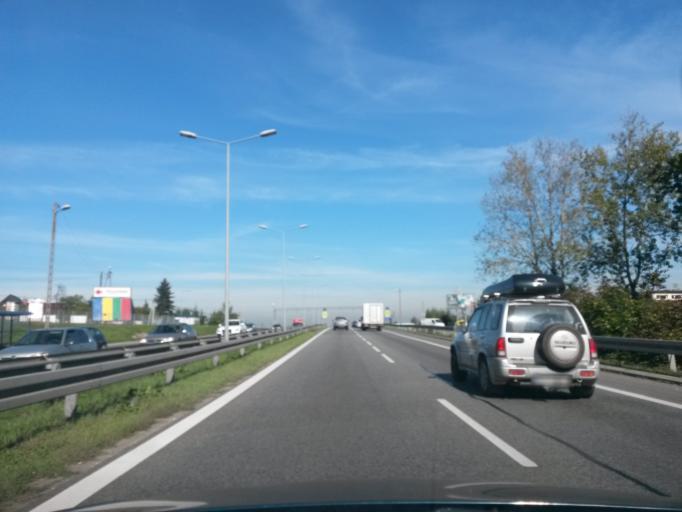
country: PL
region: Lesser Poland Voivodeship
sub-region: Powiat krakowski
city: Libertow
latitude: 49.9725
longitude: 19.9068
